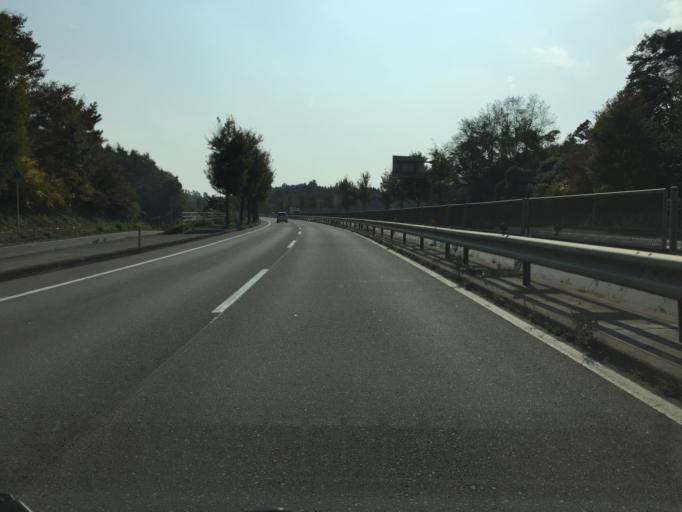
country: JP
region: Fukushima
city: Nihommatsu
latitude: 37.6189
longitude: 140.4741
